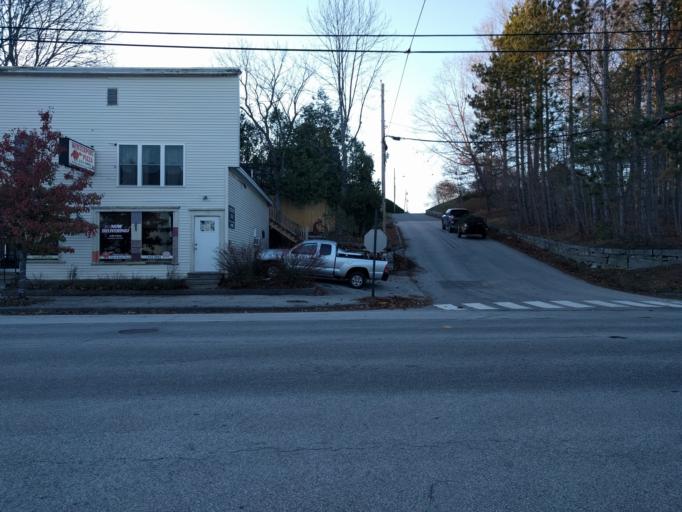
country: US
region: Maine
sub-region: Waldo County
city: Winterport
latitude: 44.6384
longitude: -68.8449
